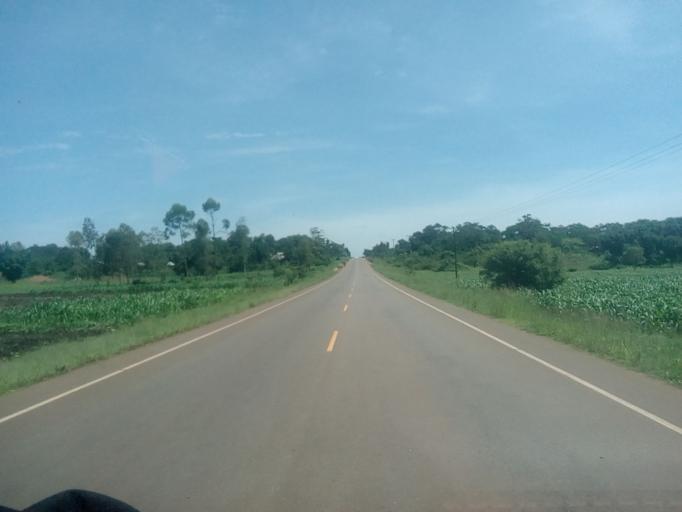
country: UG
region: Eastern Region
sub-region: Jinja District
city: Buwenge
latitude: 0.7599
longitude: 33.1479
